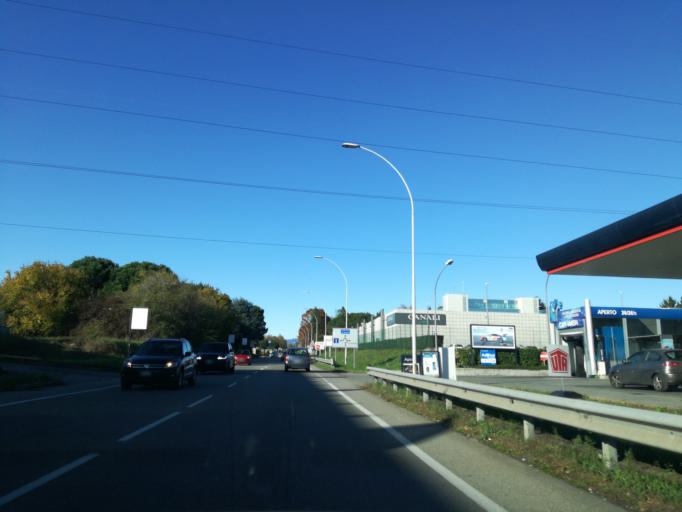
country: IT
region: Lombardy
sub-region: Provincia di Monza e Brianza
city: Sovico
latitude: 45.6502
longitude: 9.2584
